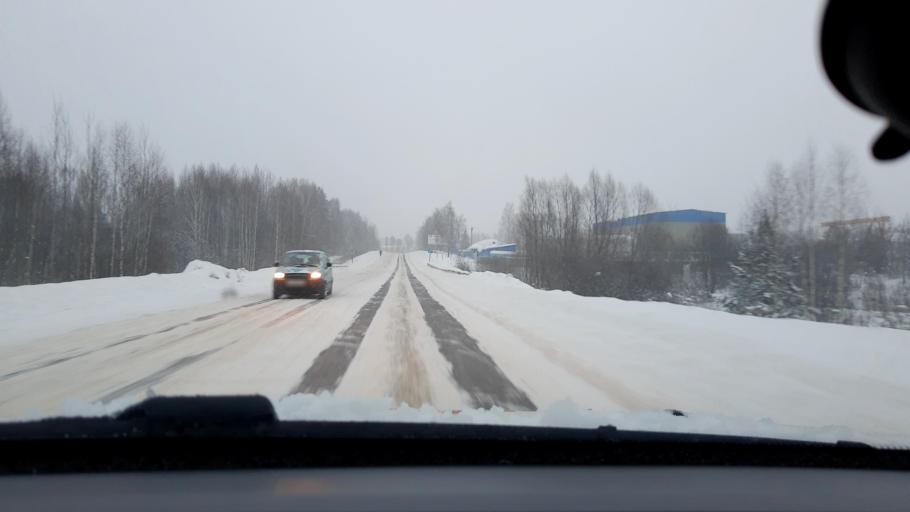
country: RU
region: Nizjnij Novgorod
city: Chkalovsk
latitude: 56.7554
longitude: 43.2153
